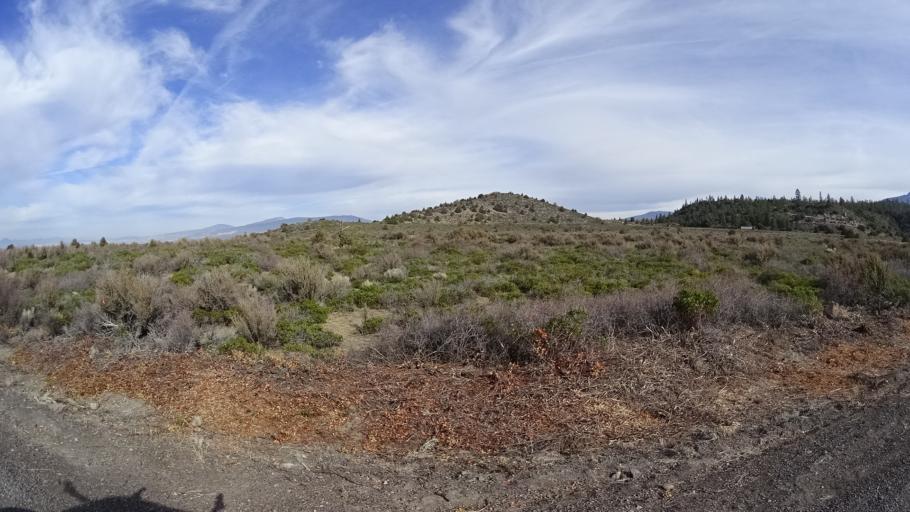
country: US
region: California
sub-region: Siskiyou County
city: Weed
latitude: 41.4761
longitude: -122.3566
